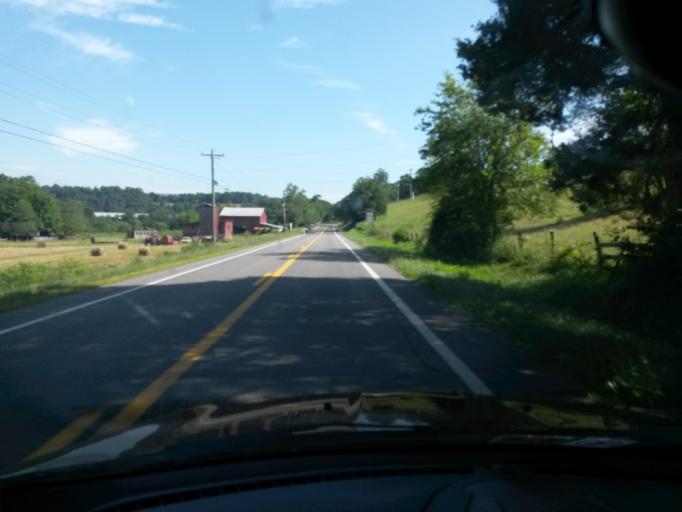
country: US
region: Virginia
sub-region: Shenandoah County
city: Basye
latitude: 38.8353
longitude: -78.8775
